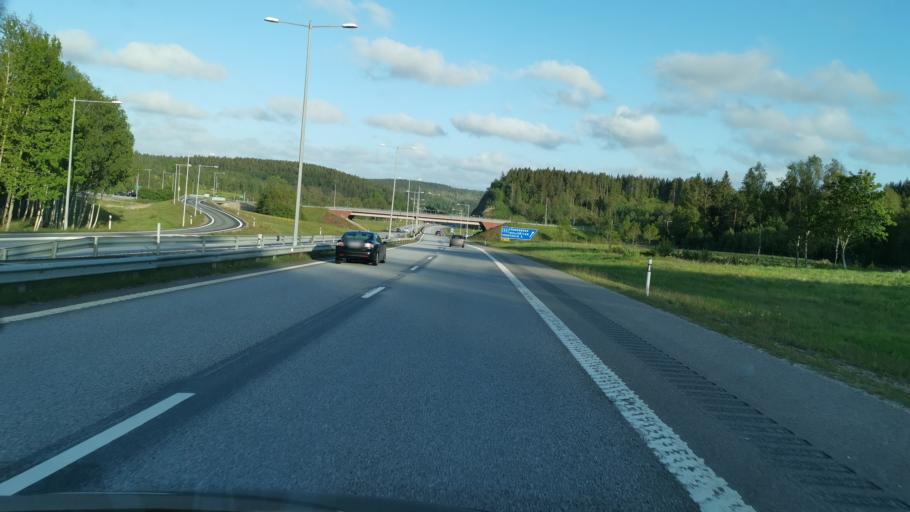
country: SE
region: Vaestra Goetaland
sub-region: Uddevalla Kommun
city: Ljungskile
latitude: 58.2929
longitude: 11.8663
